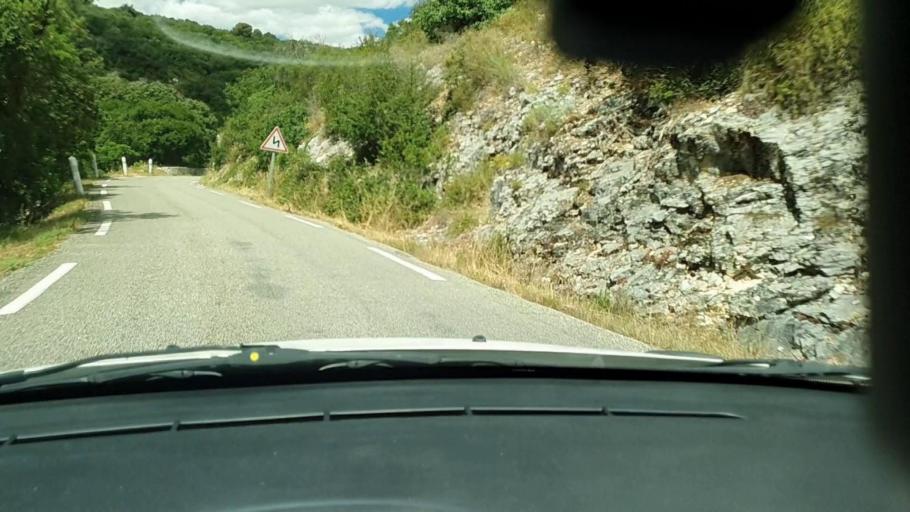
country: FR
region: Languedoc-Roussillon
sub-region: Departement du Gard
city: Cabrieres
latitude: 43.9340
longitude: 4.4741
